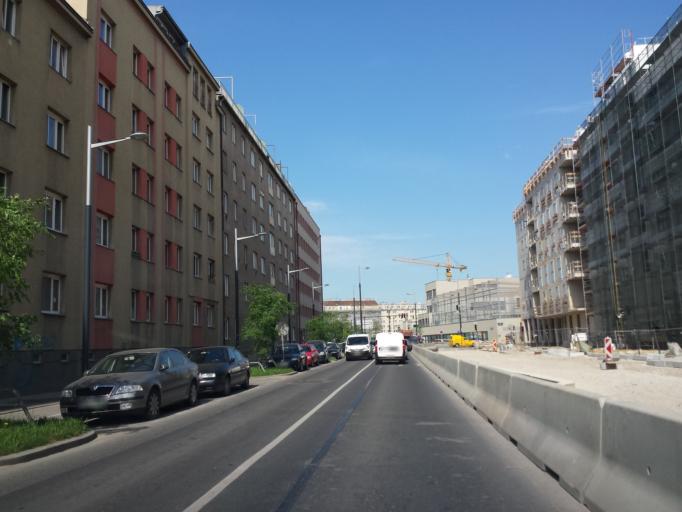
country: AT
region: Vienna
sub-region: Wien Stadt
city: Vienna
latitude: 48.1773
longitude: 16.3846
